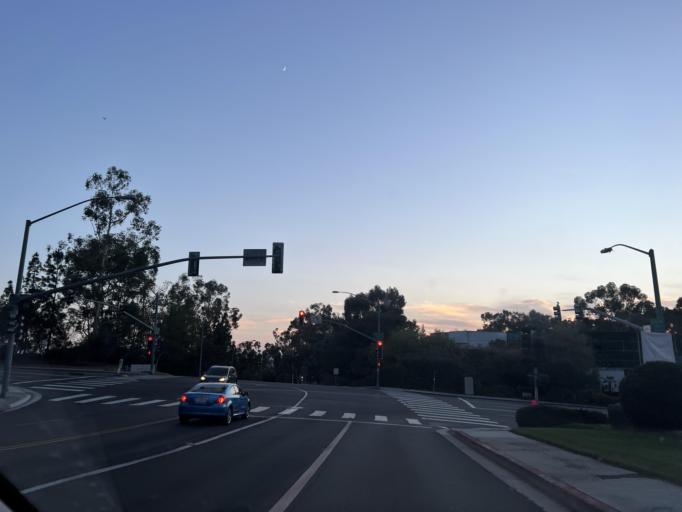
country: US
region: California
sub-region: San Diego County
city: Poway
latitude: 32.9117
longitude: -117.1095
